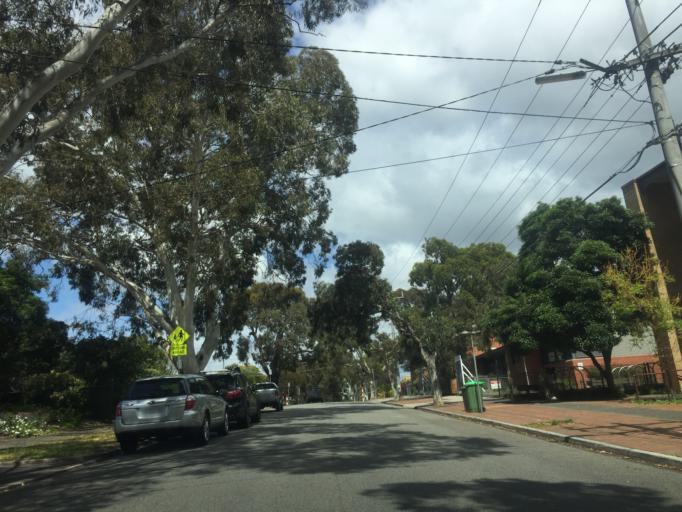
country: AU
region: Victoria
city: Ivanhoe East
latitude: -37.7737
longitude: 145.0599
